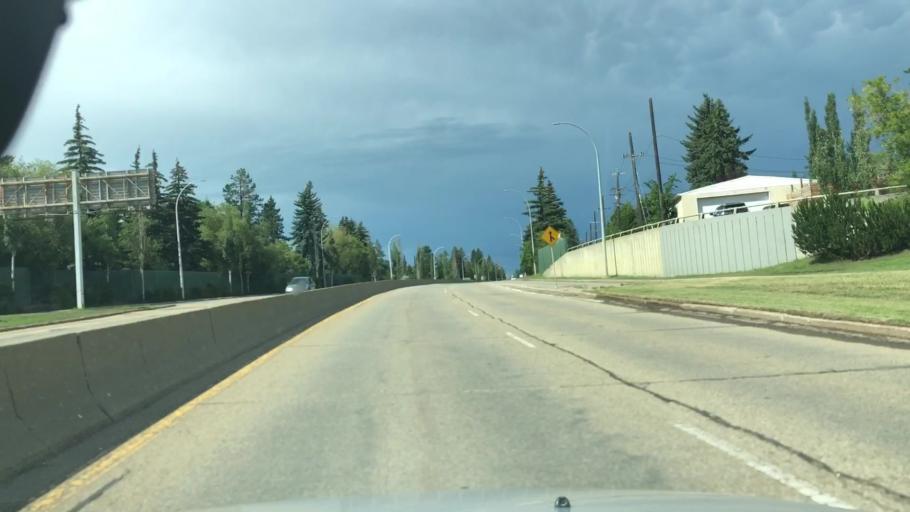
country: CA
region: Alberta
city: Edmonton
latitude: 53.5526
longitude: -113.5506
